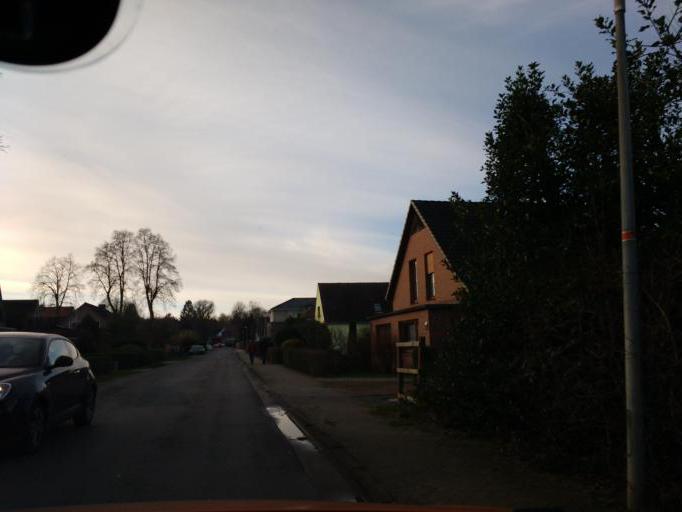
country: DE
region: Lower Saxony
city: Hude
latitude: 53.1105
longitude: 8.4700
